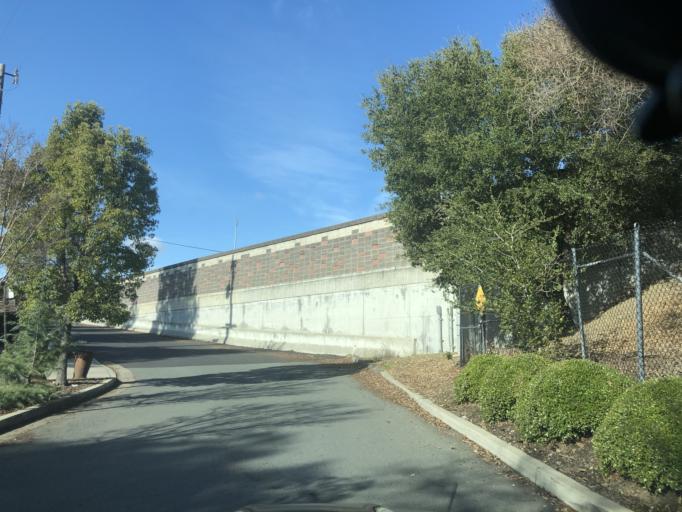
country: US
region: California
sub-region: Contra Costa County
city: Saranap
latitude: 37.8924
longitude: -122.0657
